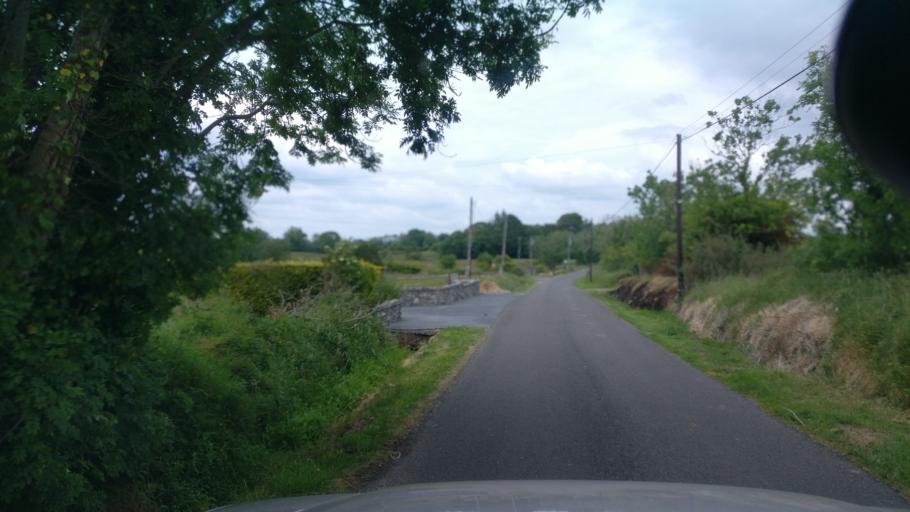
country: IE
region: Connaught
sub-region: County Galway
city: Ballinasloe
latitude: 53.2668
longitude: -8.3573
